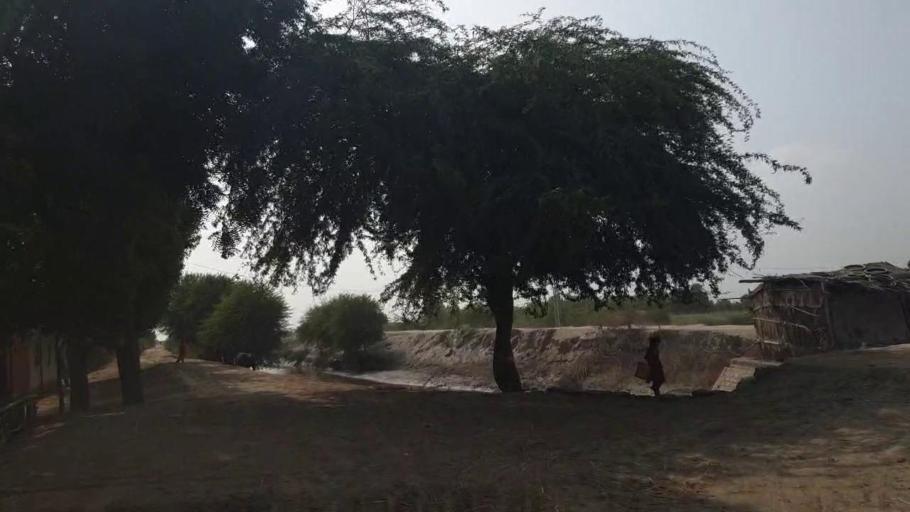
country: PK
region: Sindh
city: Badin
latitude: 24.5995
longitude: 68.7183
